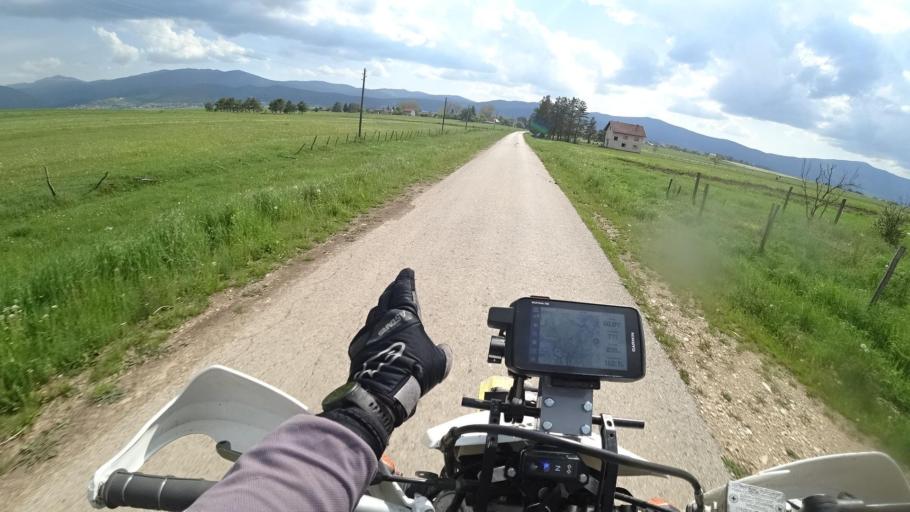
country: BA
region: Federation of Bosnia and Herzegovina
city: Glamoc
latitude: 44.0781
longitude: 16.8476
